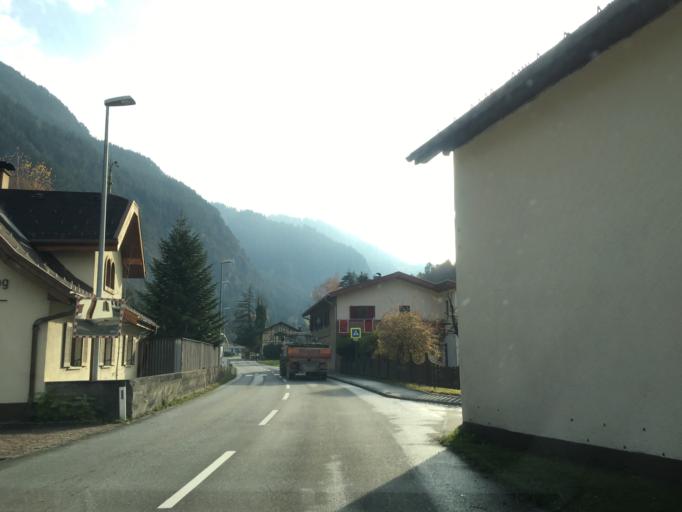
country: AT
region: Vorarlberg
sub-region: Politischer Bezirk Bludenz
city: Stallehr
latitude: 47.1306
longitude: 9.8533
